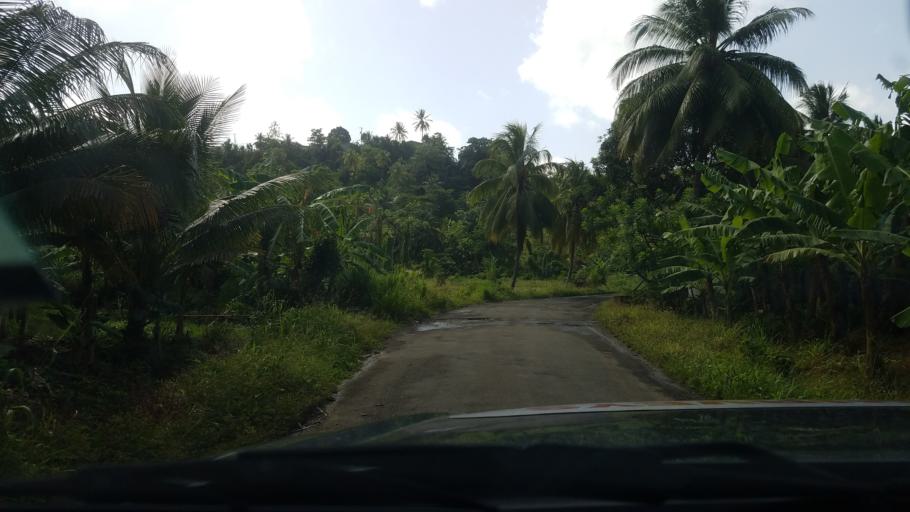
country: LC
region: Anse-la-Raye
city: Anse La Raye
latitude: 13.9543
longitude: -61.0029
